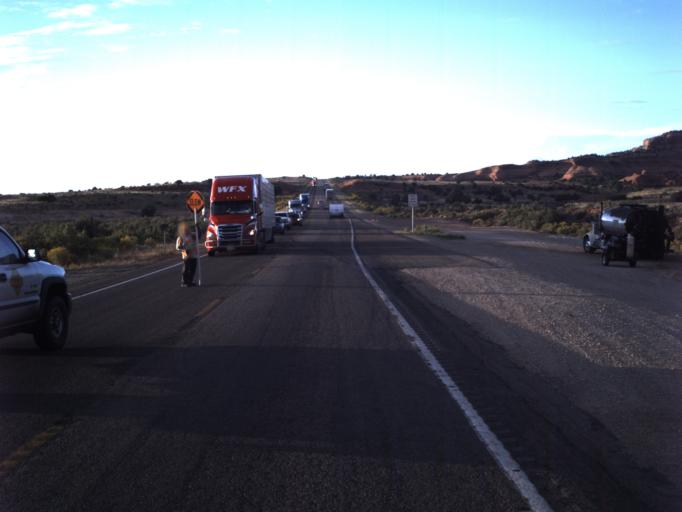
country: US
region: Utah
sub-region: San Juan County
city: Monticello
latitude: 38.2258
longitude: -109.3758
